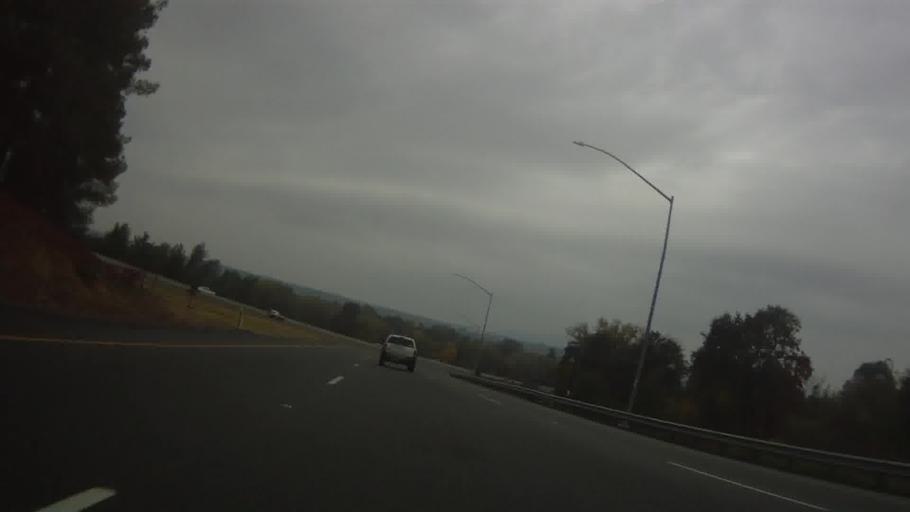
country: US
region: California
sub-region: Shasta County
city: Redding
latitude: 40.5869
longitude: -122.3627
